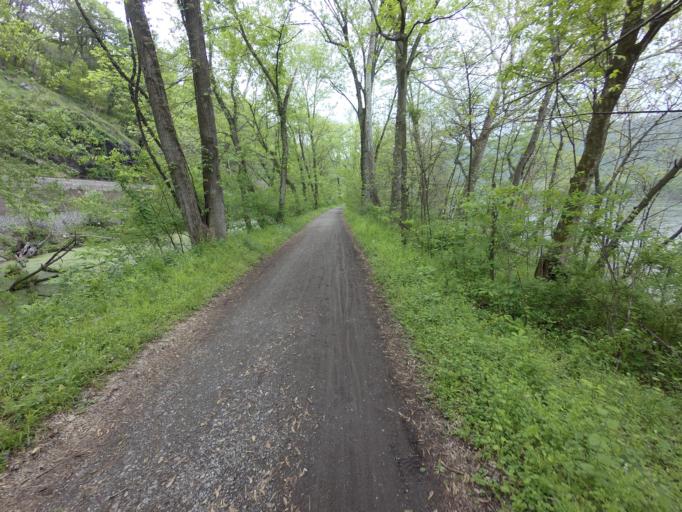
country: US
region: West Virginia
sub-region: Jefferson County
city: Bolivar
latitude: 39.3248
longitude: -77.6988
